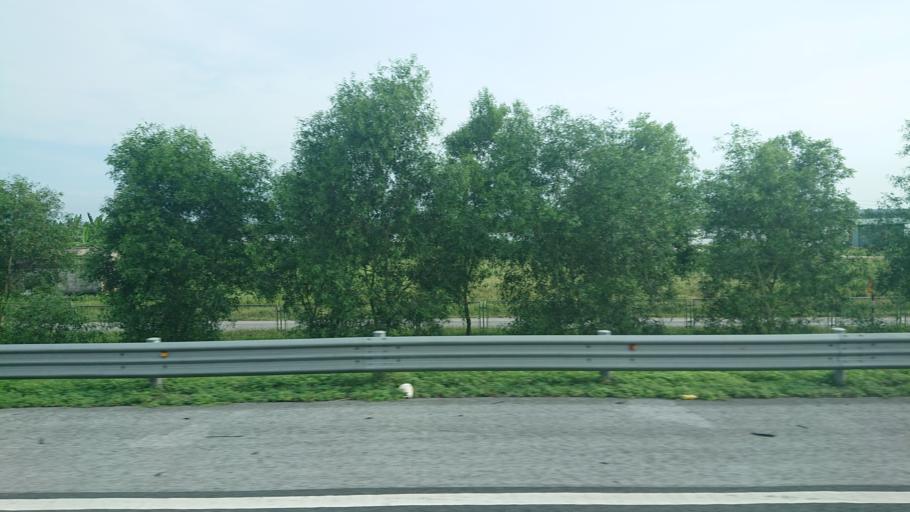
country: VN
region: Hai Phong
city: An Lao
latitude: 20.7998
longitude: 106.5349
